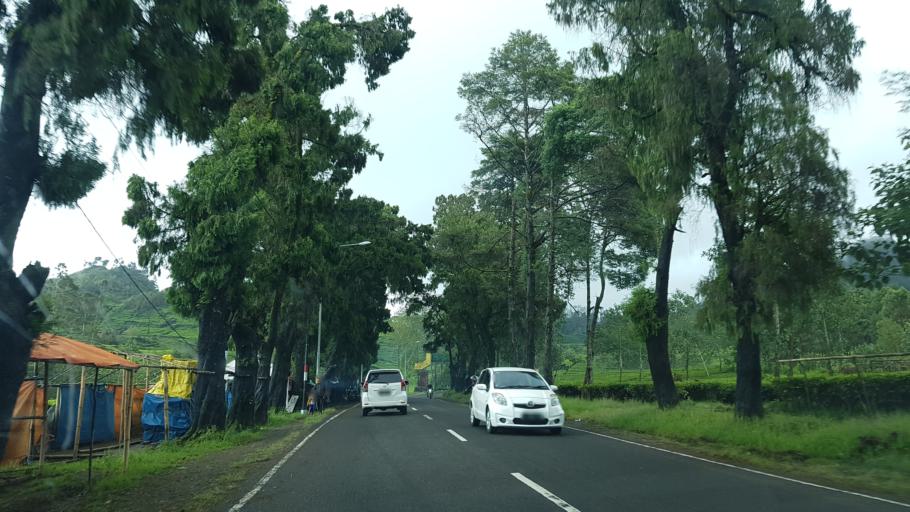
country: ID
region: West Java
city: Banjar
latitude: -7.1515
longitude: 107.3750
